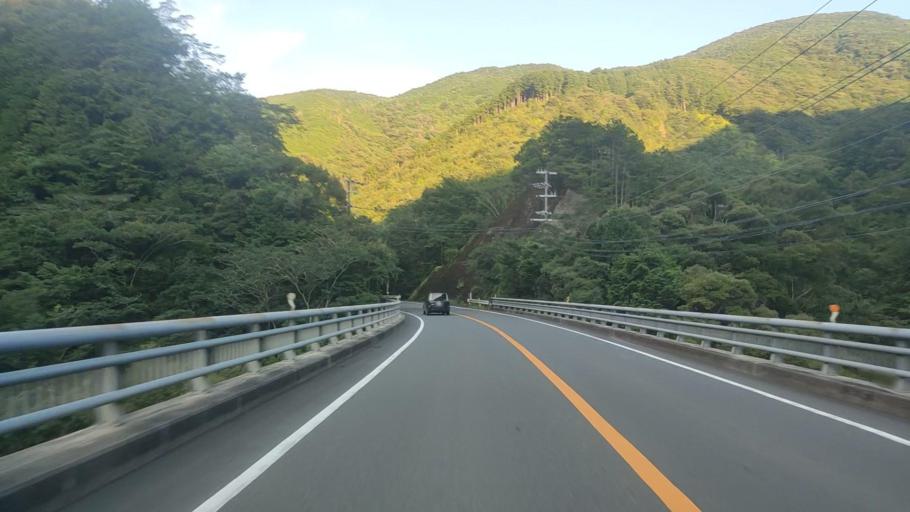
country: JP
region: Wakayama
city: Tanabe
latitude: 33.8137
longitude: 135.5632
